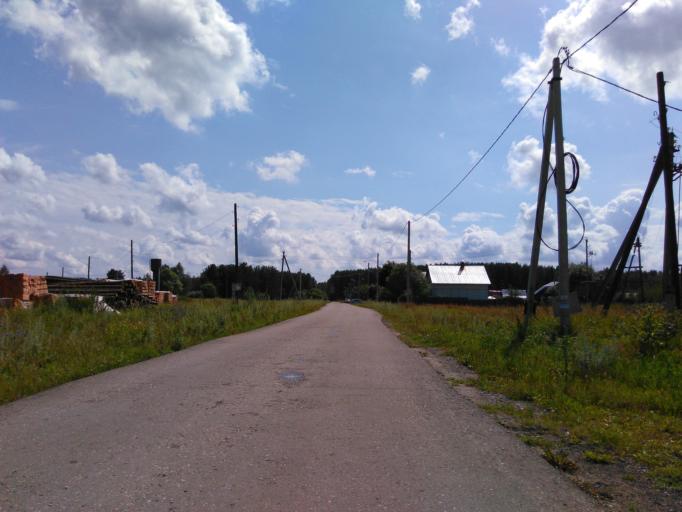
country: RU
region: Vladimir
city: Krasnyy Oktyabr'
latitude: 56.0212
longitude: 38.8056
